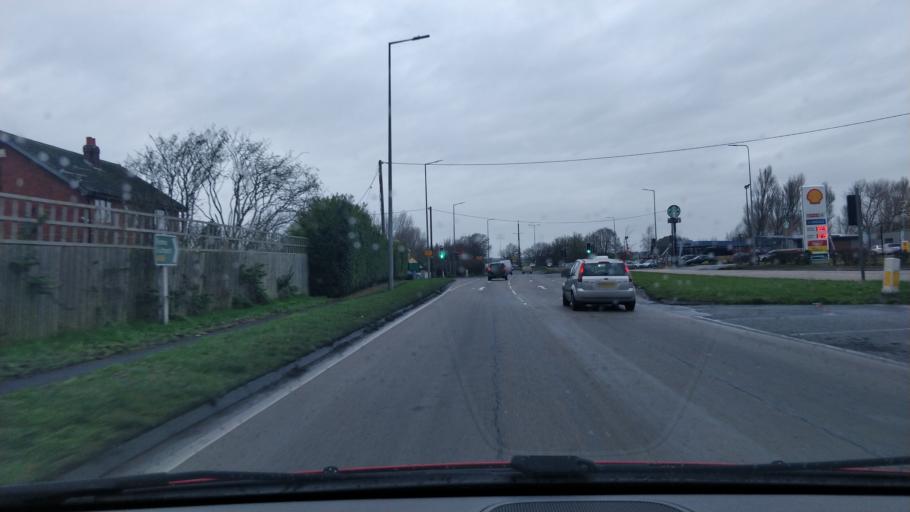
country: GB
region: England
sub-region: Sefton
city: Ince Blundell
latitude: 53.5262
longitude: -3.0317
